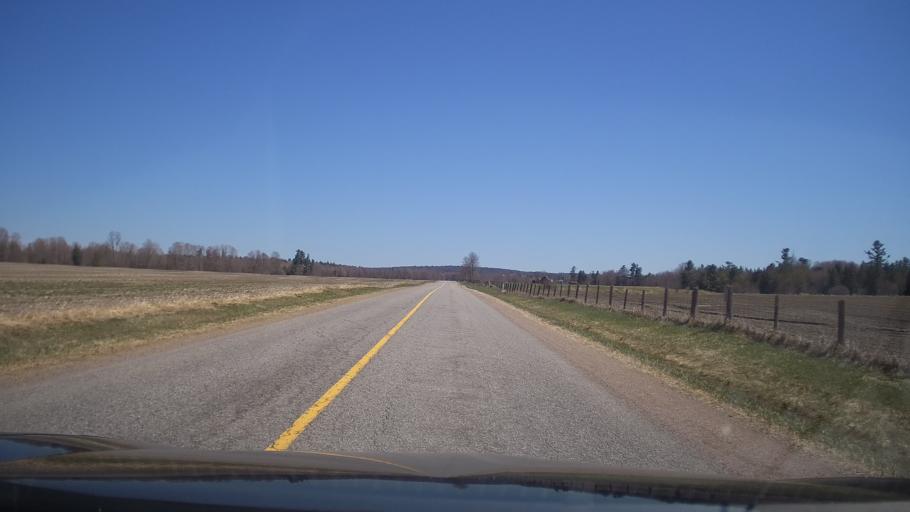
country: CA
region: Quebec
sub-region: Outaouais
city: Shawville
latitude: 45.5396
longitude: -76.3931
